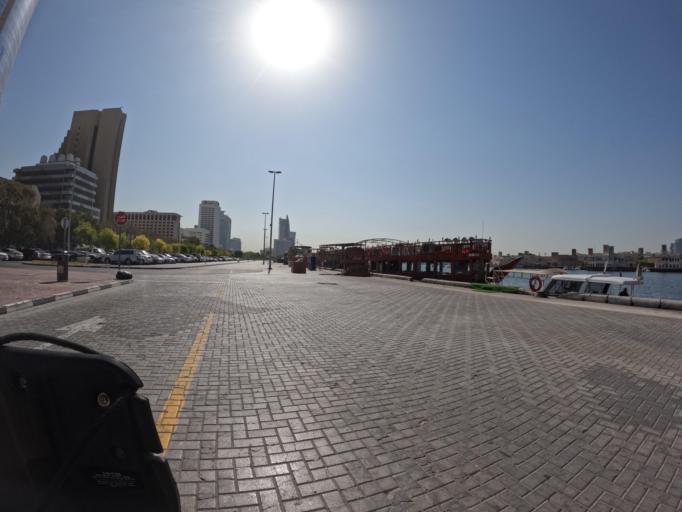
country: AE
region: Ash Shariqah
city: Sharjah
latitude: 25.2657
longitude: 55.3081
